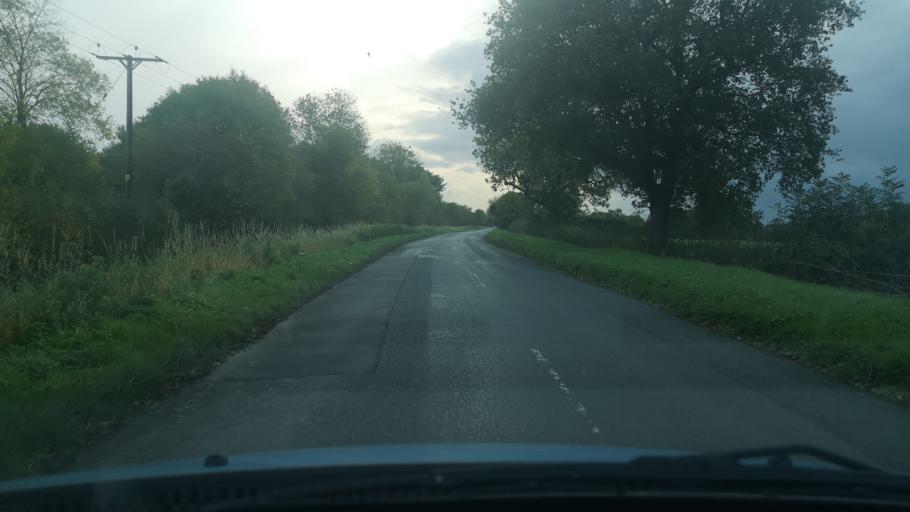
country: GB
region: England
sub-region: Doncaster
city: Hatfield
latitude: 53.6163
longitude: -0.9952
